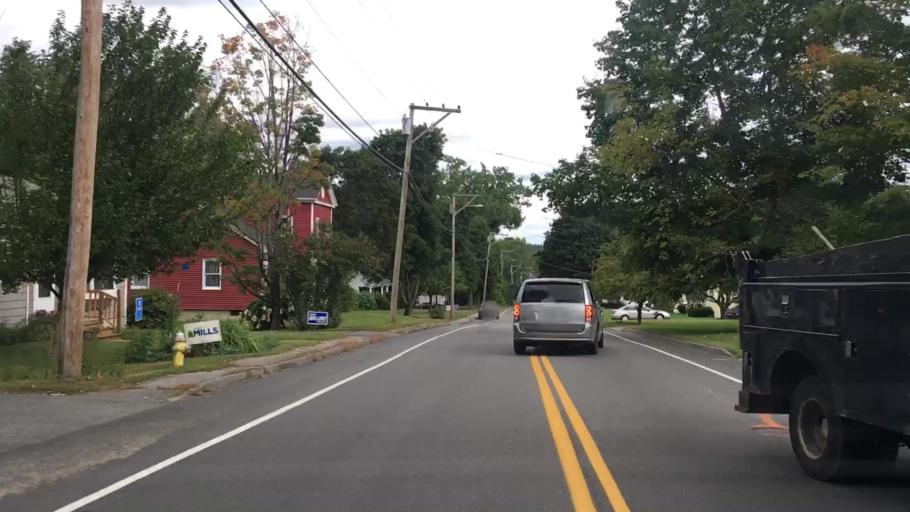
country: US
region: Maine
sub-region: Kennebec County
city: Hallowell
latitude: 44.2675
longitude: -69.7909
